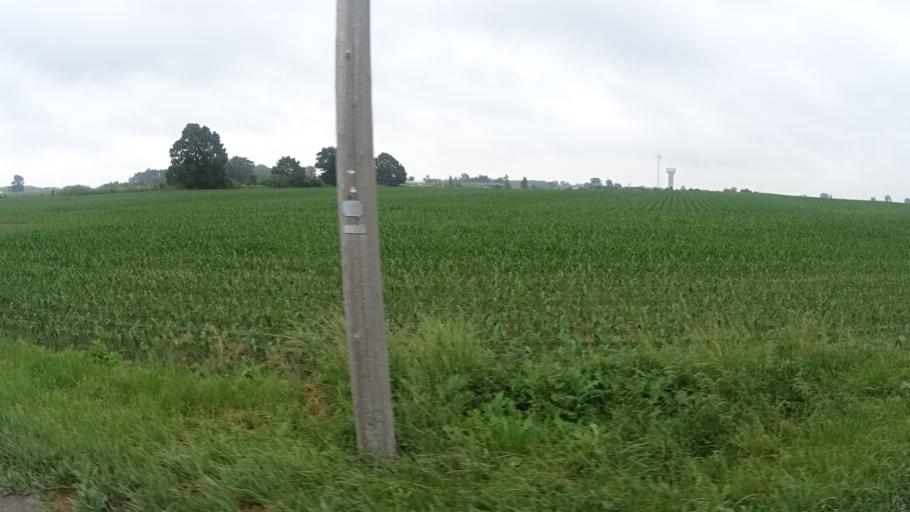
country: US
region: Ohio
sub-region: Huron County
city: Bellevue
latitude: 41.3472
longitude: -82.7619
